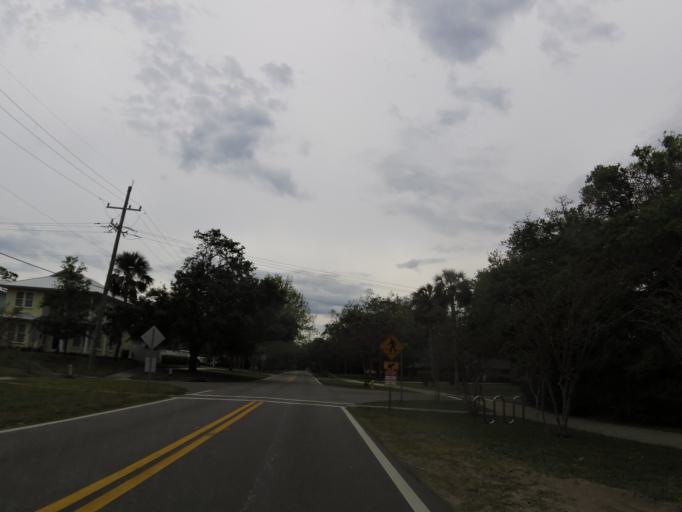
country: US
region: Florida
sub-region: Duval County
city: Atlantic Beach
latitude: 30.3360
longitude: -81.4026
